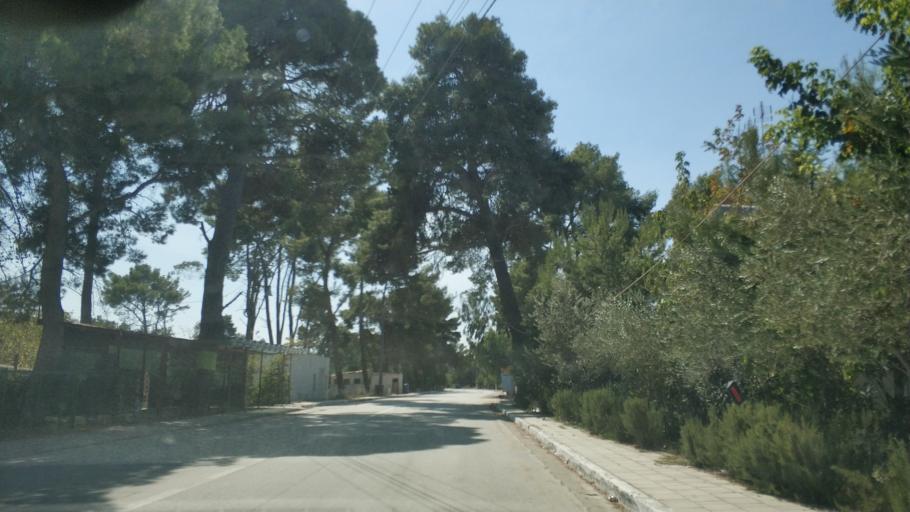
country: AL
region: Fier
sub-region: Rrethi i Lushnjes
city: Divjake
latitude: 40.9698
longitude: 19.4793
